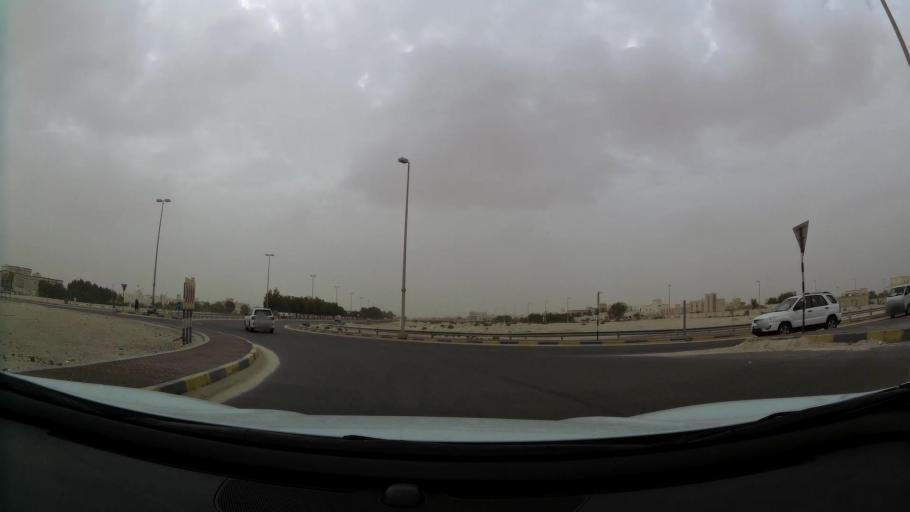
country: AE
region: Abu Dhabi
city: Abu Dhabi
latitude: 24.4011
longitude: 54.7168
